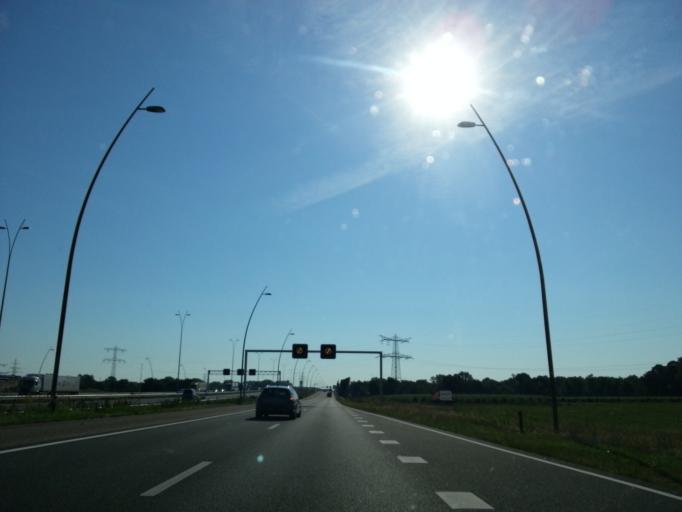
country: NL
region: North Brabant
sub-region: Gemeente Waalre
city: Waalre
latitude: 51.4052
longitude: 5.4557
